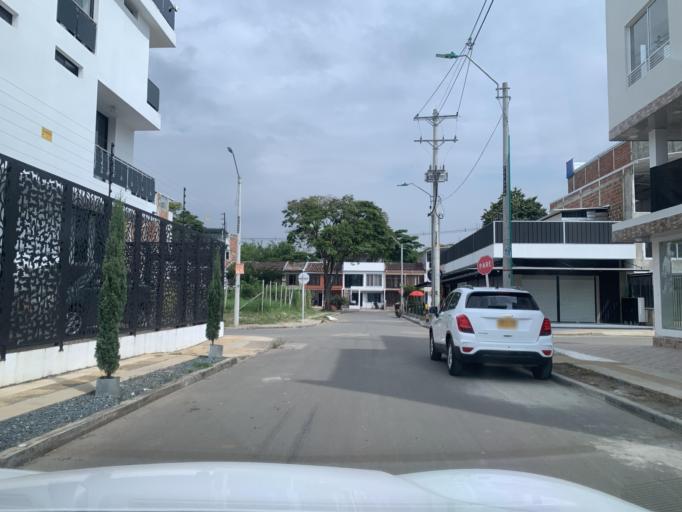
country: CO
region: Valle del Cauca
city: Cali
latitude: 3.3939
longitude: -76.5205
